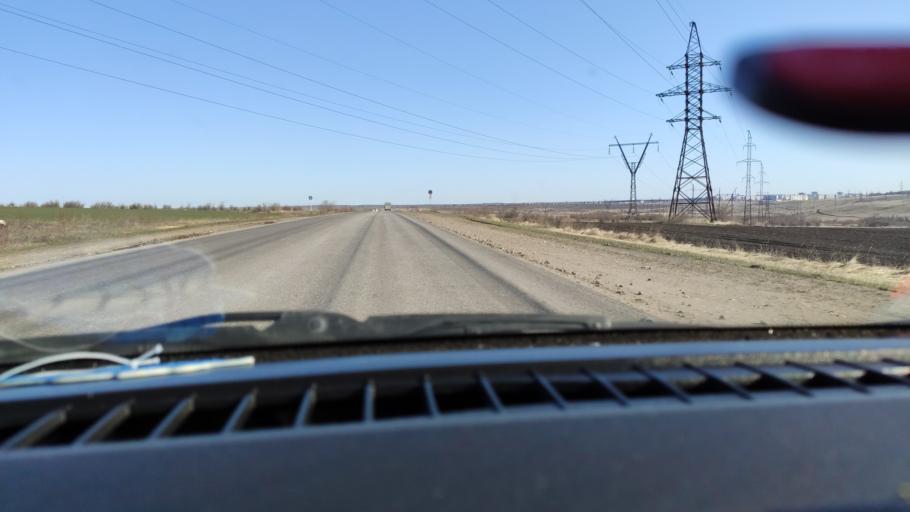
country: RU
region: Samara
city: Varlamovo
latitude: 53.0826
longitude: 48.3545
